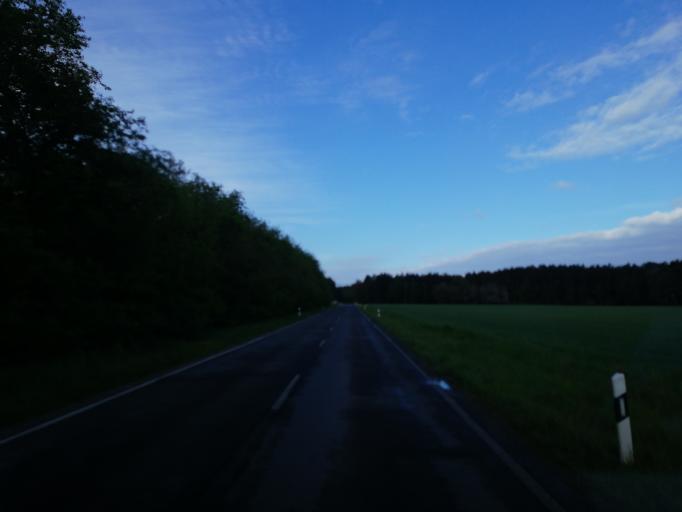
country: DE
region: Brandenburg
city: Sallgast
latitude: 51.5929
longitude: 13.7739
